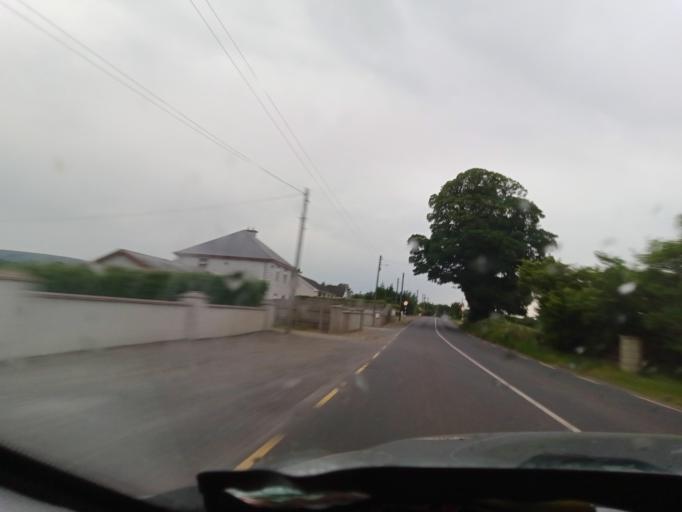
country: IE
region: Leinster
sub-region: Uibh Fhaili
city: Tullamore
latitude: 53.1473
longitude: -7.5071
